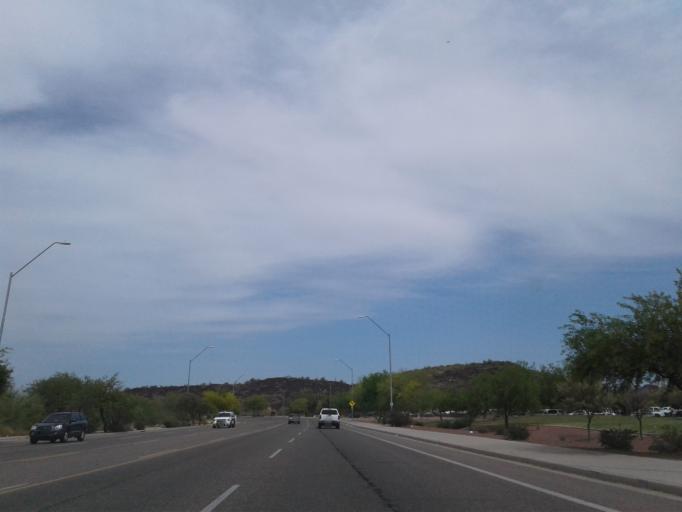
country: US
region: Arizona
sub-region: Maricopa County
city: Peoria
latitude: 33.6984
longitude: -112.1335
